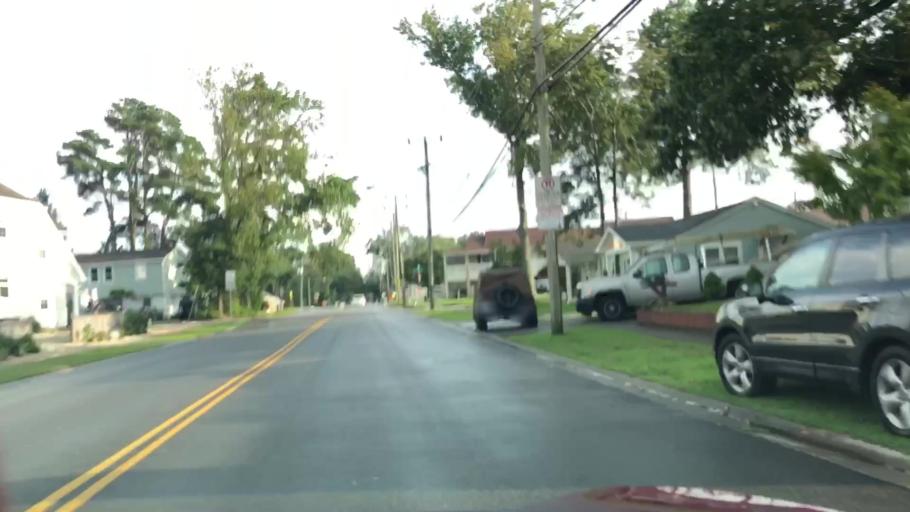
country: US
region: Virginia
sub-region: City of Virginia Beach
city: Virginia Beach
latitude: 36.8388
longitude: -75.9797
